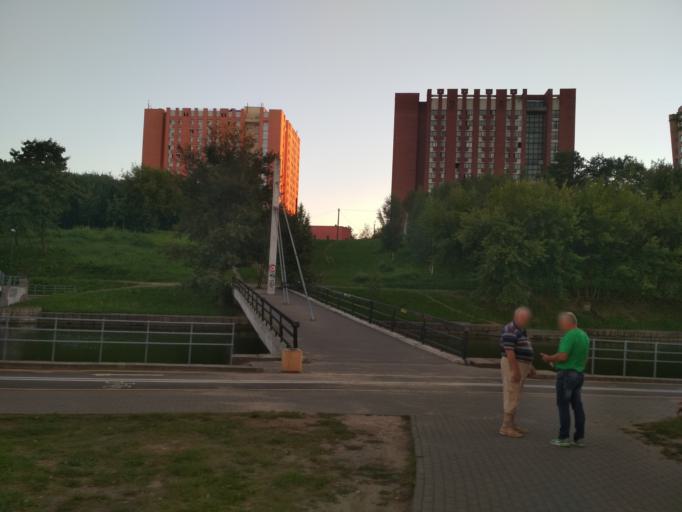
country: BY
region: Minsk
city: Minsk
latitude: 53.8910
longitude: 27.5664
